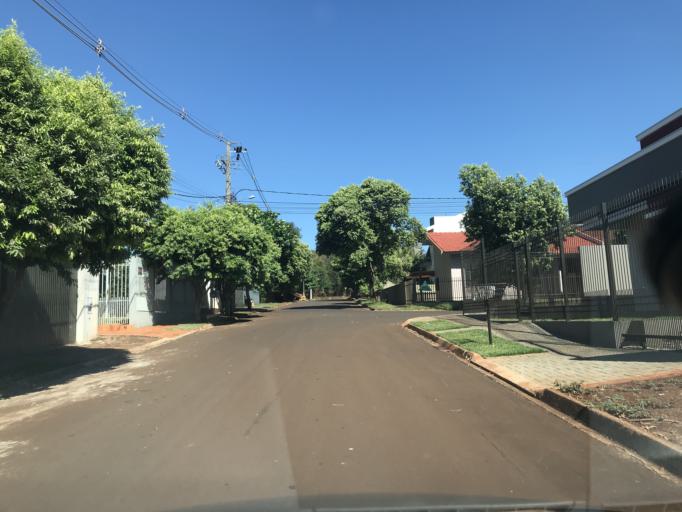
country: BR
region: Parana
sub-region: Palotina
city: Palotina
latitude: -24.2783
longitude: -53.8264
